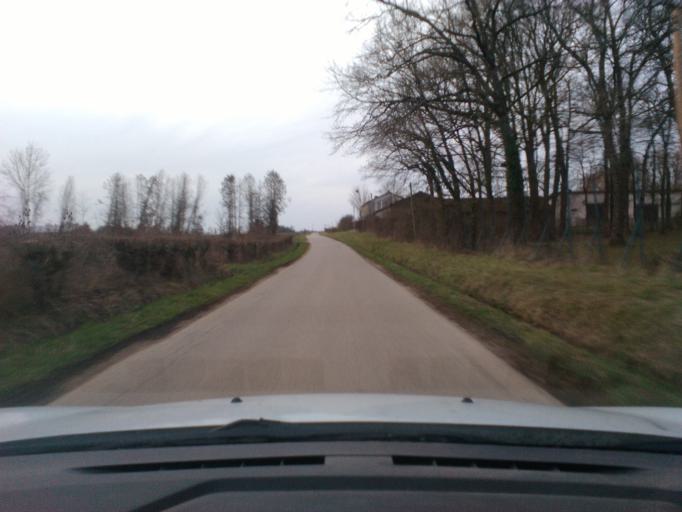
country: FR
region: Lorraine
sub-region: Departement des Vosges
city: Mirecourt
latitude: 48.2910
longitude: 6.1069
